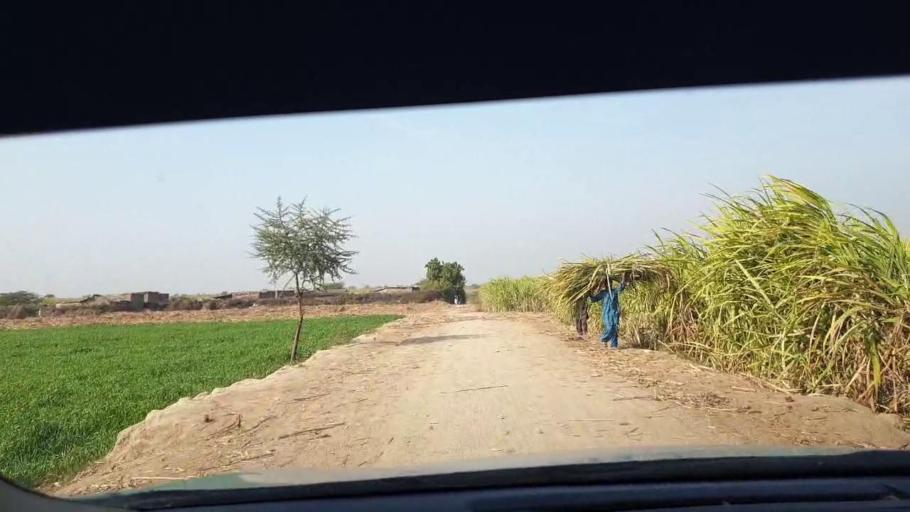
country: PK
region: Sindh
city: Tando Adam
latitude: 25.7650
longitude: 68.7212
